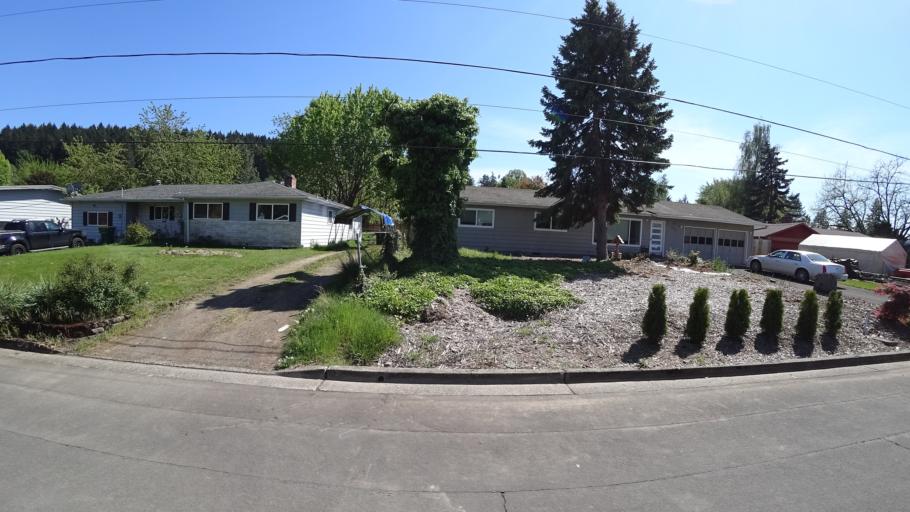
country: US
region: Oregon
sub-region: Washington County
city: Aloha
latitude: 45.4768
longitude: -122.8474
